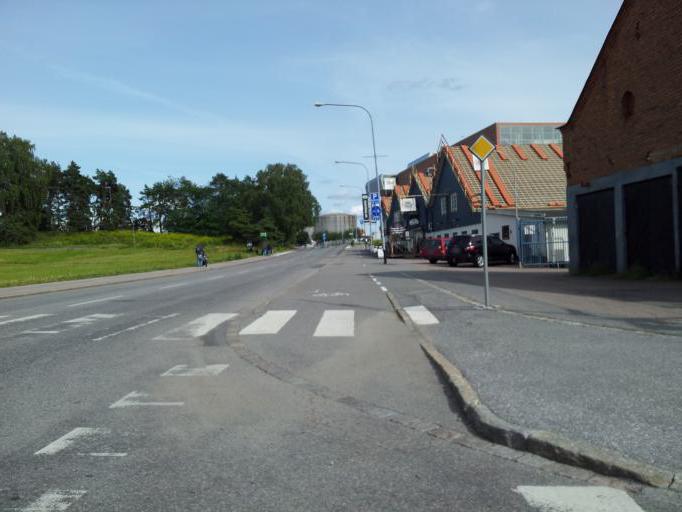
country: SE
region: Uppsala
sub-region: Uppsala Kommun
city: Uppsala
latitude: 59.8545
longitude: 17.6710
